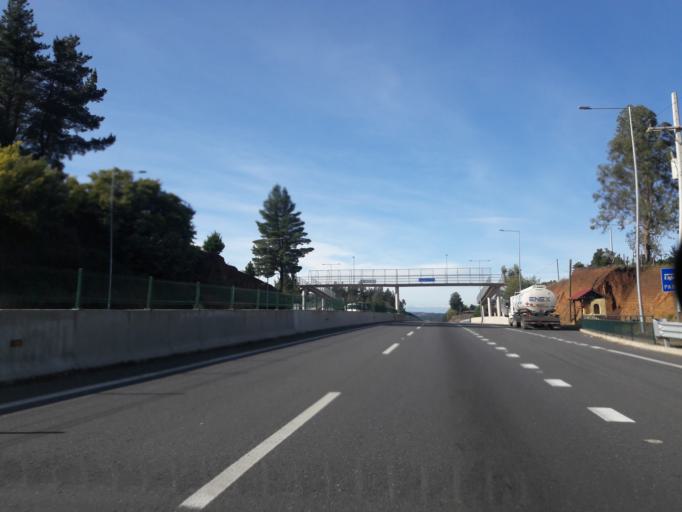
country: CL
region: Biobio
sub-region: Provincia de Biobio
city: Yumbel
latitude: -36.9632
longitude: -72.7104
